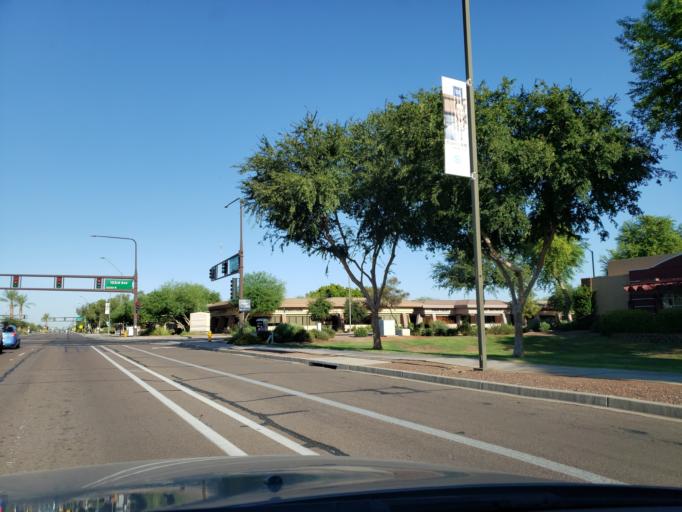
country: US
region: Arizona
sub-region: Maricopa County
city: Tolleson
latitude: 33.4647
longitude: -112.2806
